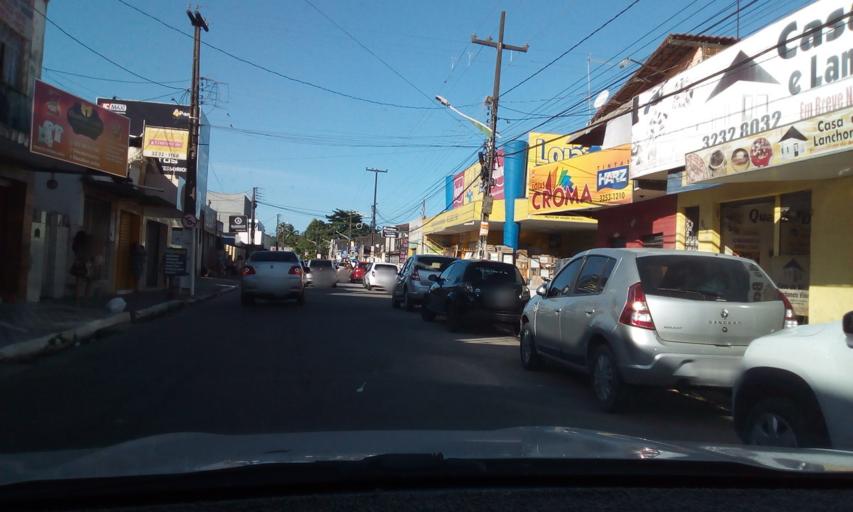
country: BR
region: Paraiba
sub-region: Bayeux
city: Bayeux
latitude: -7.1284
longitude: -34.9299
